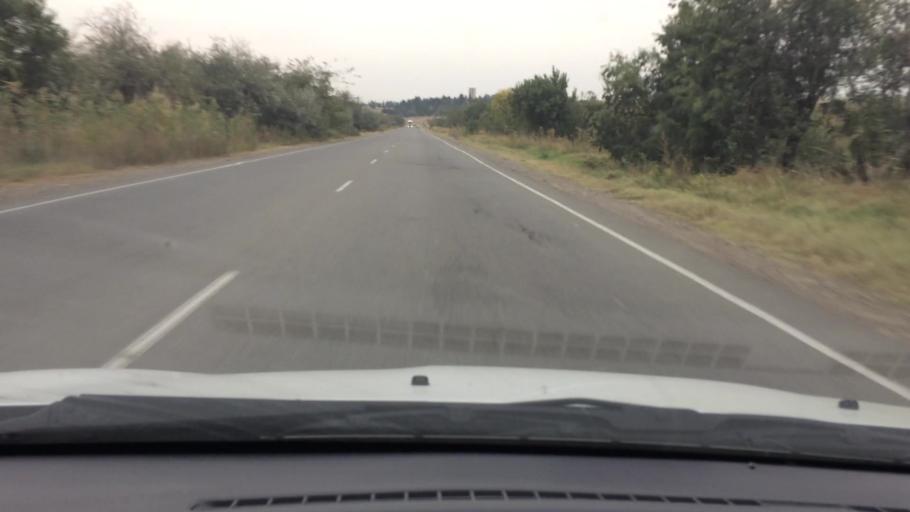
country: GE
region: Kvemo Kartli
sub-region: Marneuli
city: Marneuli
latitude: 41.5332
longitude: 44.7769
